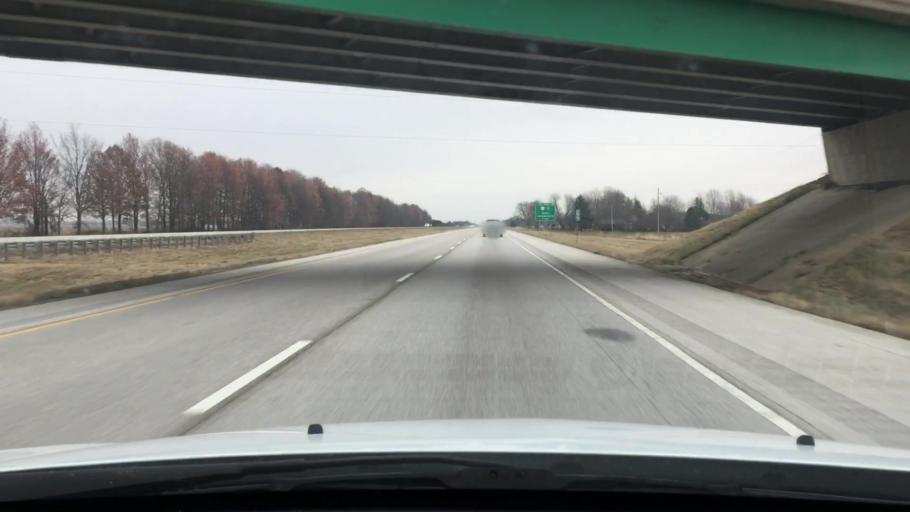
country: US
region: Illinois
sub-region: Morgan County
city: South Jacksonville
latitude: 39.6802
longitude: -90.3259
